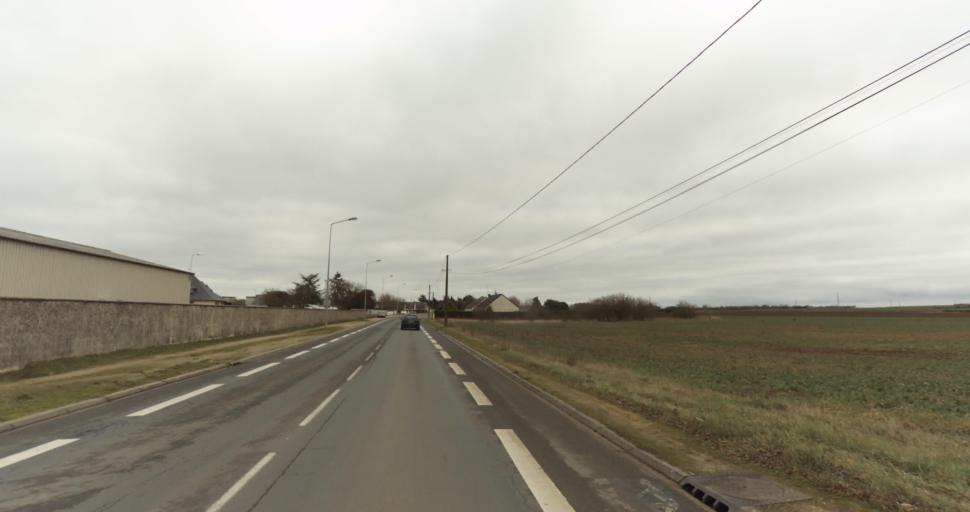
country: FR
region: Pays de la Loire
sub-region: Departement de Maine-et-Loire
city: Doue-la-Fontaine
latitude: 47.1872
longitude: -0.2713
